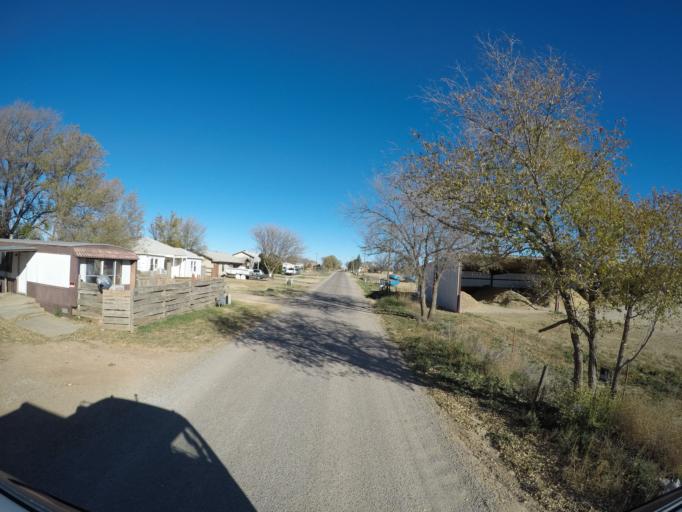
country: US
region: New Mexico
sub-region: Curry County
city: Clovis
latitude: 34.4439
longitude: -103.1996
